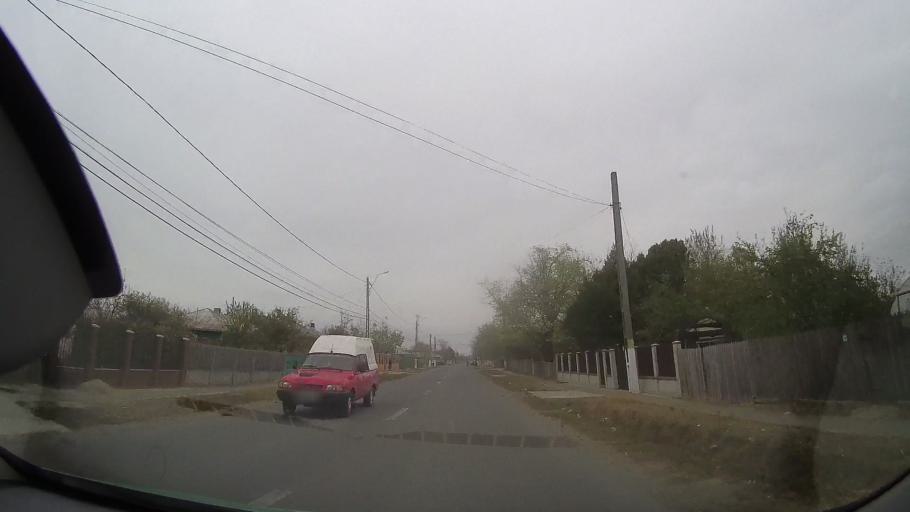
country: RO
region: Braila
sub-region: Comuna Budesti
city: Tataru
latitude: 44.8461
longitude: 27.4278
